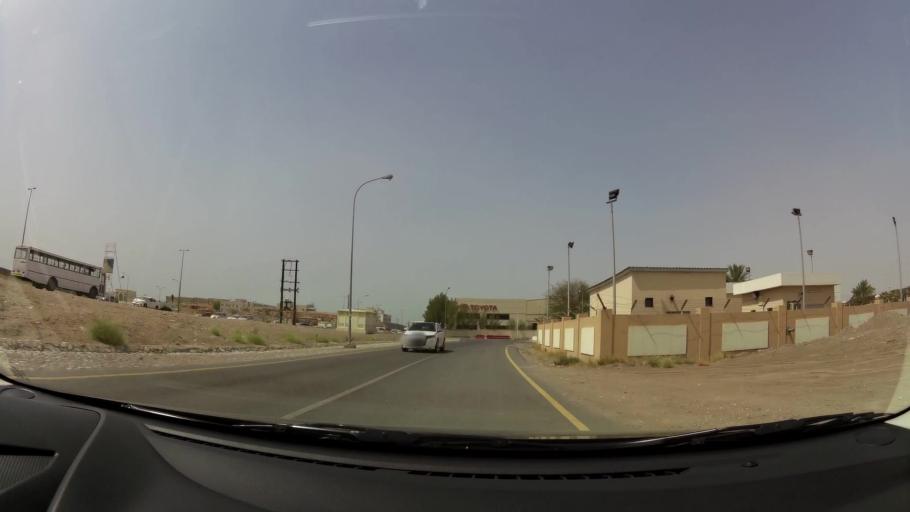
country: OM
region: Muhafazat Masqat
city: Bawshar
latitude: 23.5701
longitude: 58.3808
